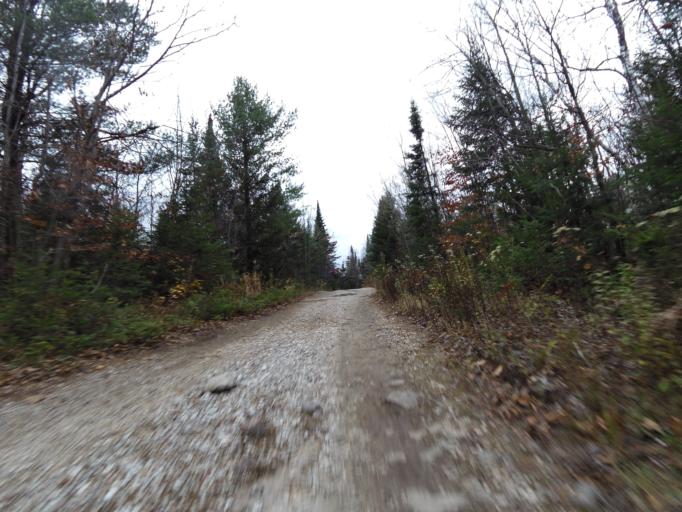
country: CA
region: Quebec
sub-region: Outaouais
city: Wakefield
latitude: 45.5564
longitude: -75.9802
